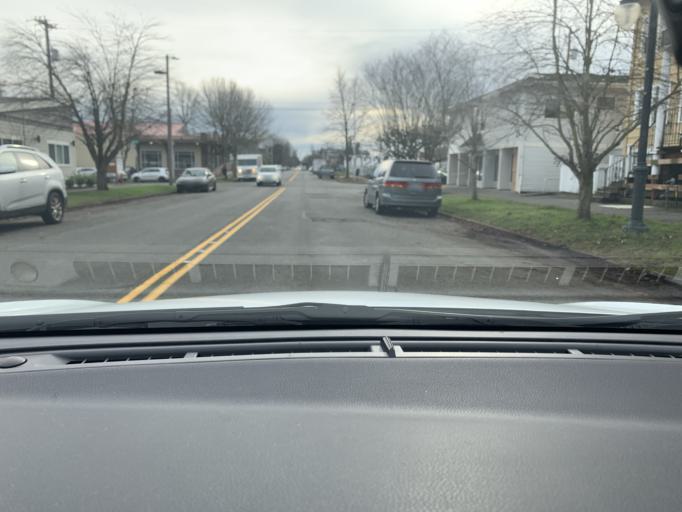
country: US
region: Washington
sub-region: Pierce County
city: Tacoma
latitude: 47.2537
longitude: -122.4506
